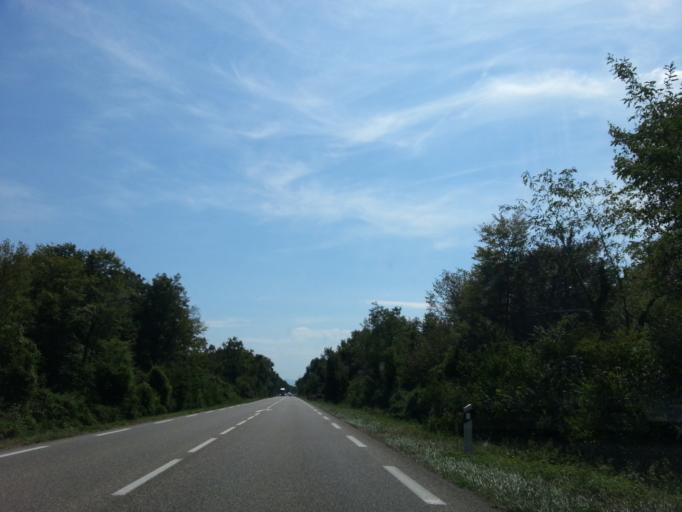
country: FR
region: Alsace
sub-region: Departement du Haut-Rhin
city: Widensolen
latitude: 48.0447
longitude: 7.4669
